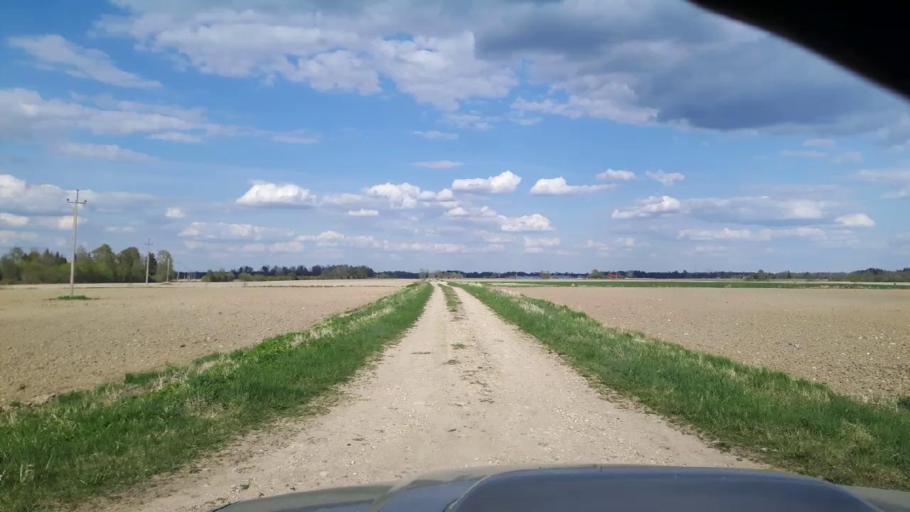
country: EE
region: Paernumaa
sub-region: Sindi linn
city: Sindi
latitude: 58.4331
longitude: 24.7410
